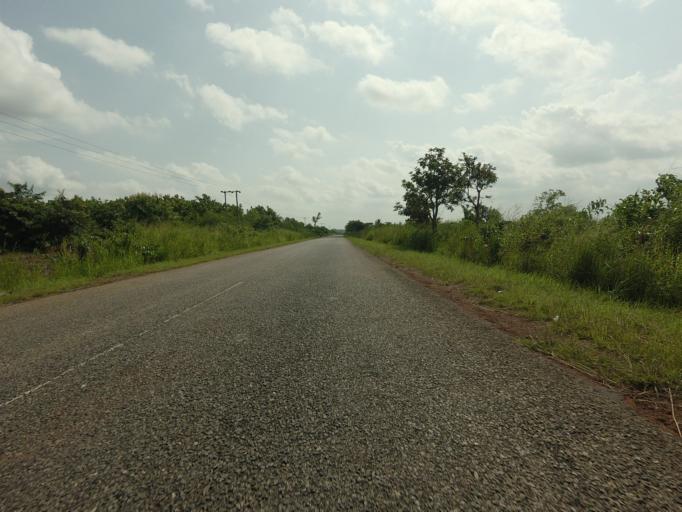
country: TG
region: Maritime
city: Tsevie
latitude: 6.3924
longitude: 0.8202
